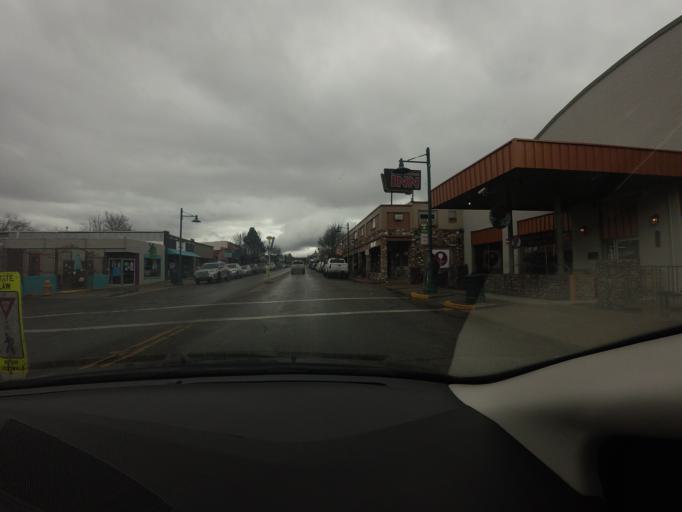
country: US
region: Arizona
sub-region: Yavapai County
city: Cottonwood
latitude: 34.7491
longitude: -112.0274
